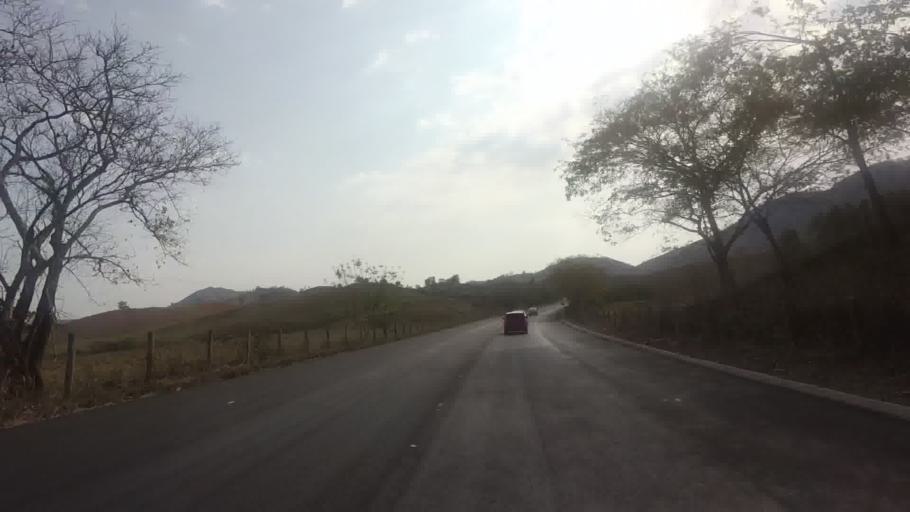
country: BR
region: Rio de Janeiro
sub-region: Bom Jesus Do Itabapoana
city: Bom Jesus do Itabapoana
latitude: -21.1952
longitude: -41.7001
